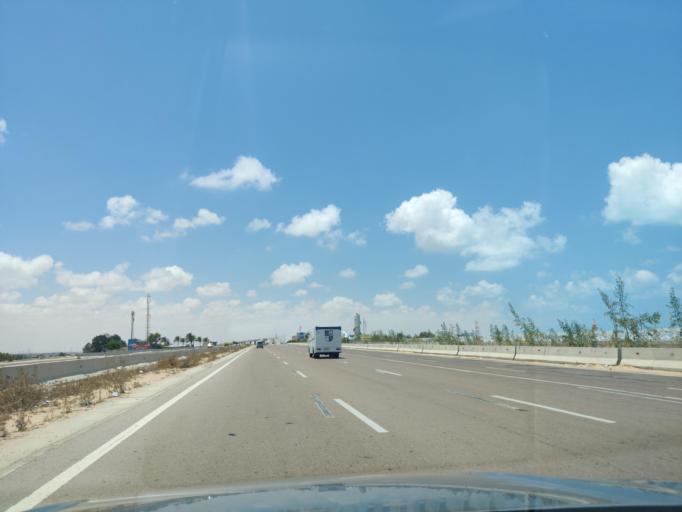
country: EG
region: Muhafazat Matruh
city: Al `Alamayn
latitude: 30.8126
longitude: 29.0705
